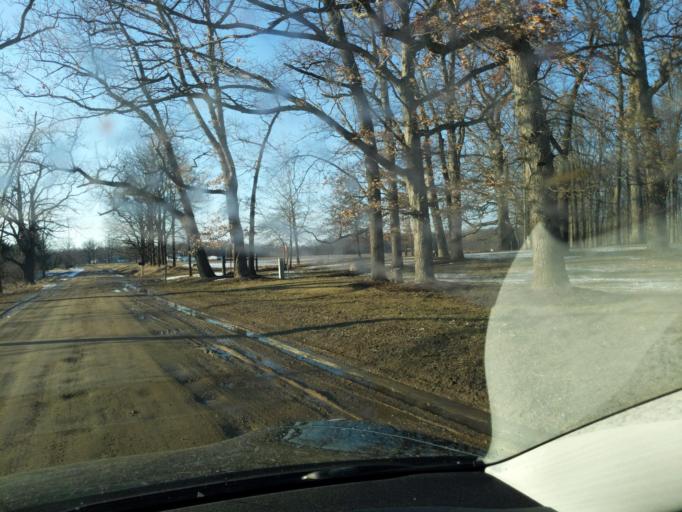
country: US
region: Michigan
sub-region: Ingham County
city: Stockbridge
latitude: 42.5278
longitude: -84.2631
